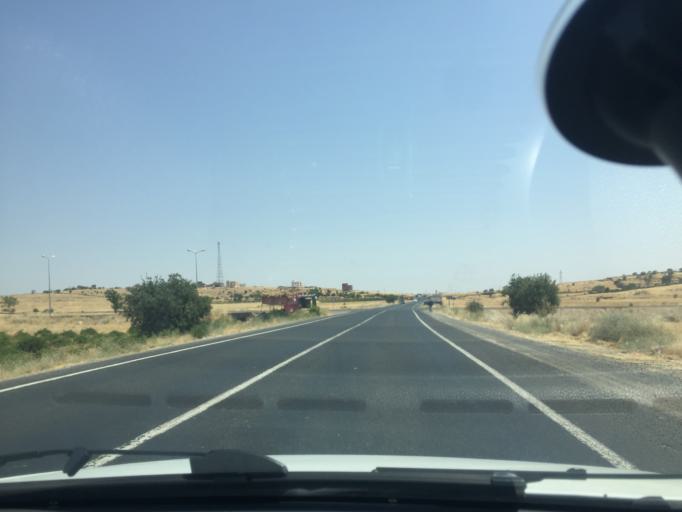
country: TR
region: Mardin
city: Acirli
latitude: 37.4458
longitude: 41.2815
